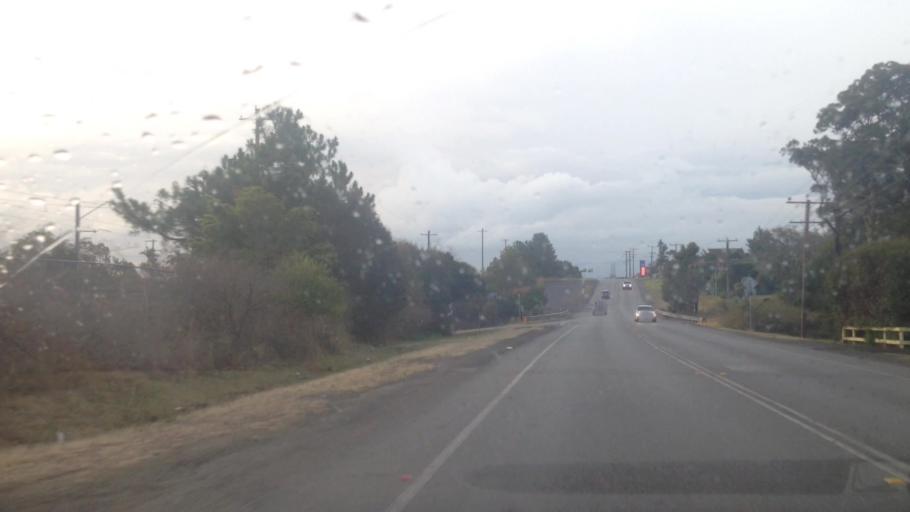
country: AU
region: New South Wales
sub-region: Wyong Shire
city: Charmhaven
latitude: -33.1789
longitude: 151.4873
